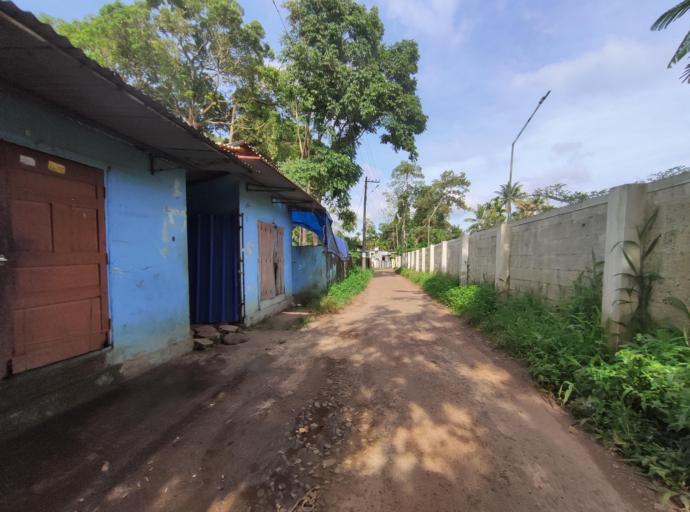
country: IN
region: Kerala
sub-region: Alappuzha
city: Vayalar
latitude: 9.6931
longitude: 76.3372
